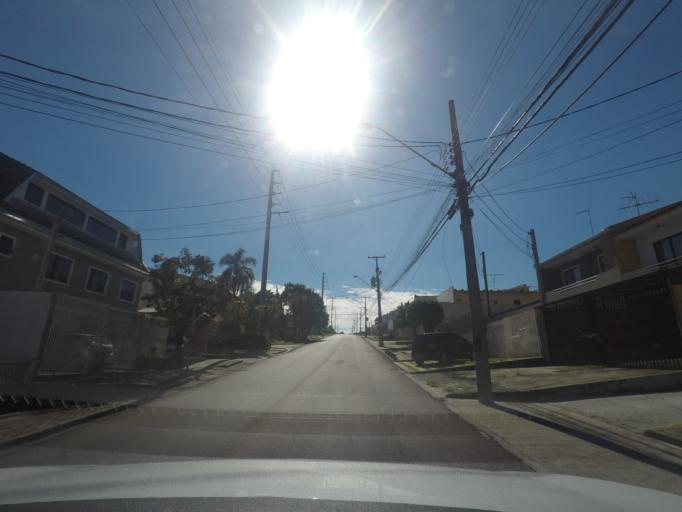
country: BR
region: Parana
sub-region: Sao Jose Dos Pinhais
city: Sao Jose dos Pinhais
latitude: -25.5043
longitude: -49.2773
